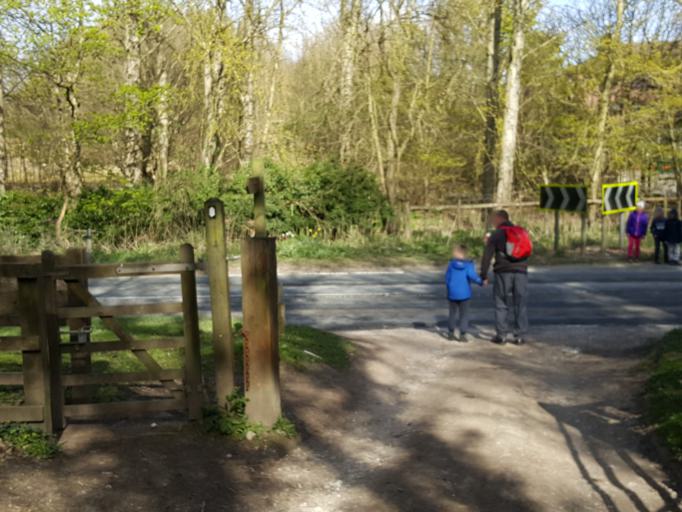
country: GB
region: England
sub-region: East Riding of Yorkshire
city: North Ferriby
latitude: 53.7334
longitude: -0.5243
